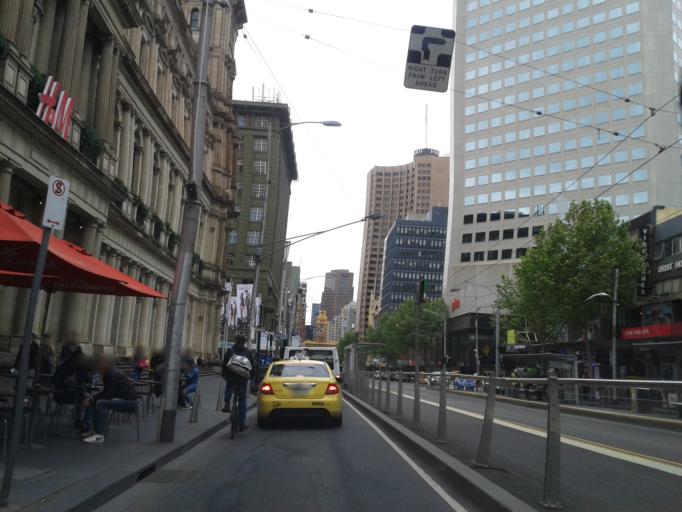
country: AU
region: Victoria
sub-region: Melbourne
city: Melbourne
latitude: -37.8134
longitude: 144.9629
